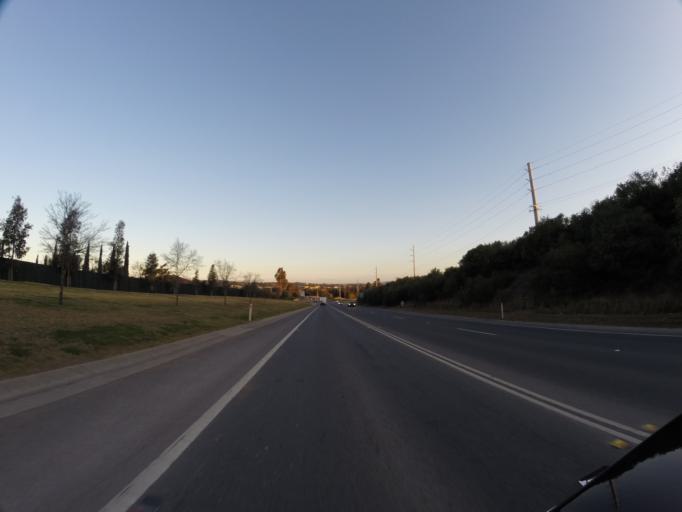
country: AU
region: New South Wales
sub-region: Camden
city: Narellan
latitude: -34.0236
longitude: 150.7263
